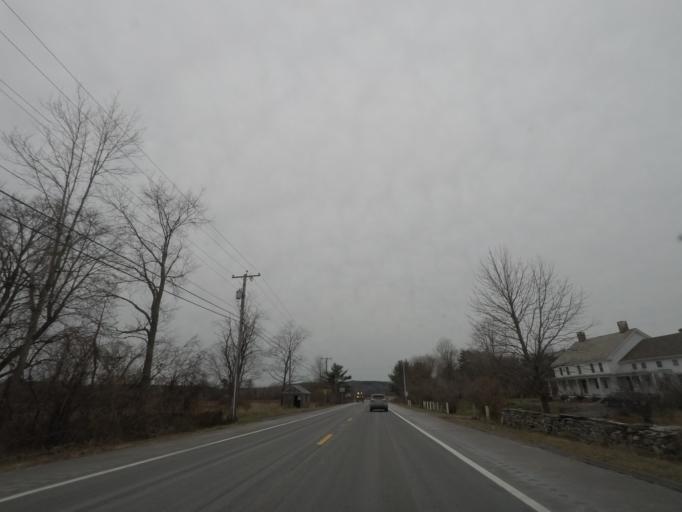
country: US
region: Massachusetts
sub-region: Berkshire County
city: Lanesborough
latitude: 42.5392
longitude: -73.3397
